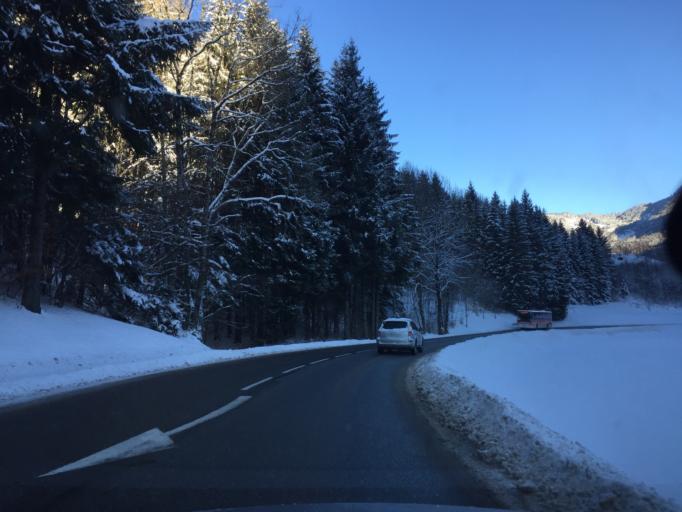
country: FR
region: Rhone-Alpes
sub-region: Departement de la Haute-Savoie
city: Abondance
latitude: 46.3027
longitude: 6.6750
